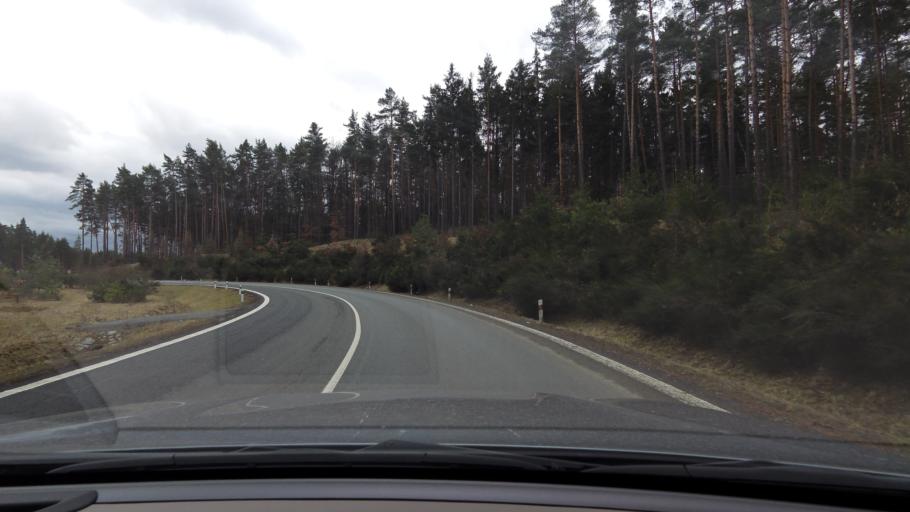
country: CZ
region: Plzensky
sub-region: Okres Plzen-Sever
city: Tremosna
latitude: 49.8038
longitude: 13.3870
